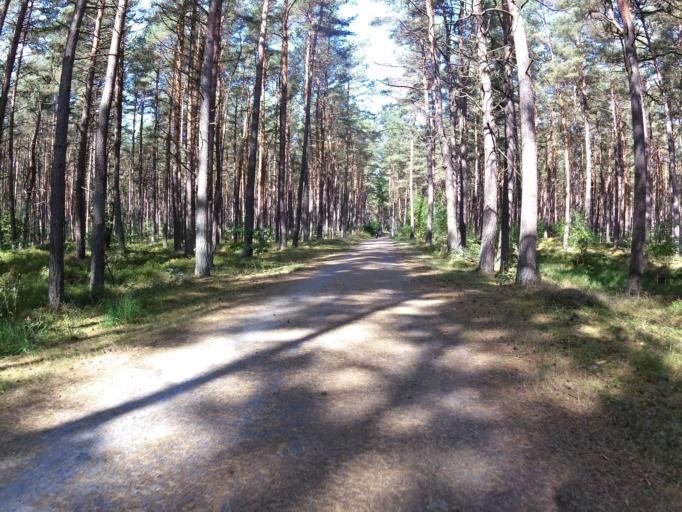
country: DE
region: Mecklenburg-Vorpommern
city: Karlshagen
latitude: 54.1050
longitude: 13.8543
